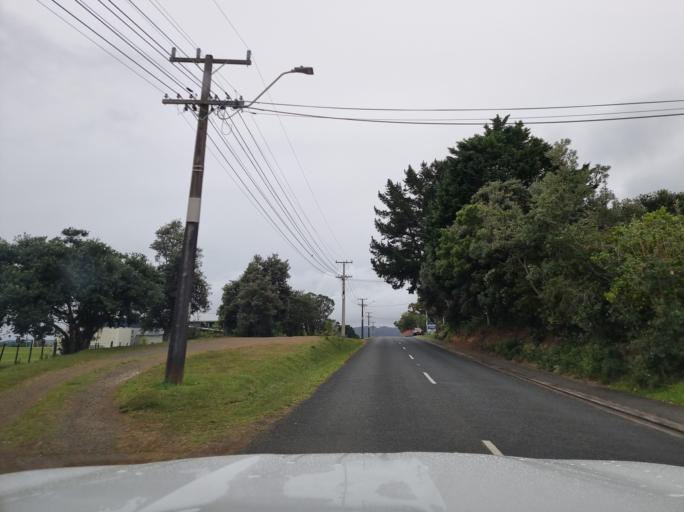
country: NZ
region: Northland
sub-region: Whangarei
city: Whangarei
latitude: -35.7716
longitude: 174.3661
